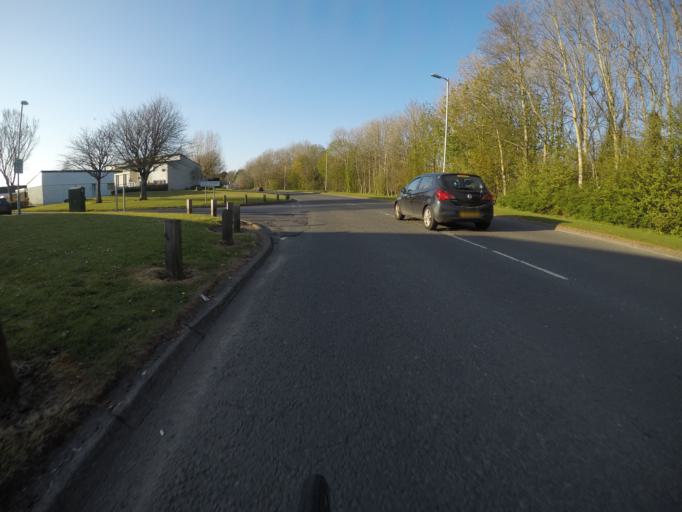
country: GB
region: Scotland
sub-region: North Ayrshire
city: Kilwinning
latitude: 55.6495
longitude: -4.7076
